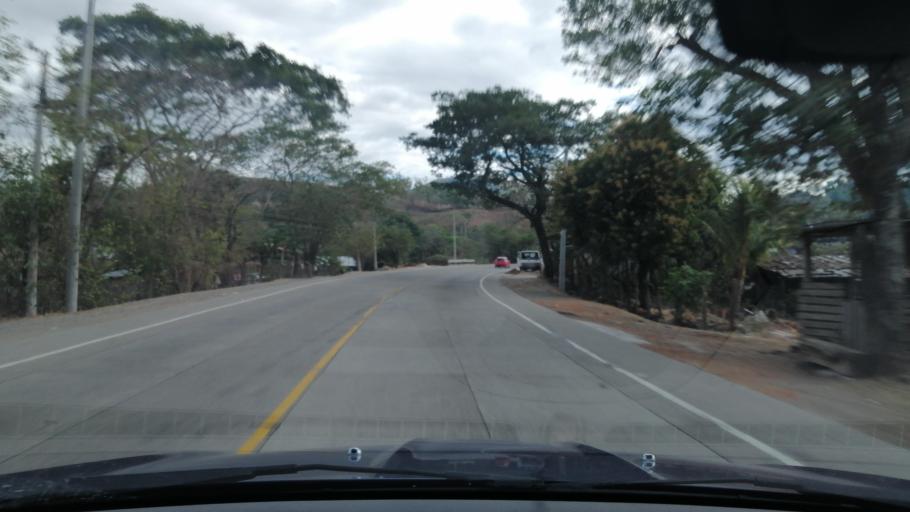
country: SV
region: Santa Ana
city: Texistepeque
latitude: 14.0823
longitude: -89.4997
